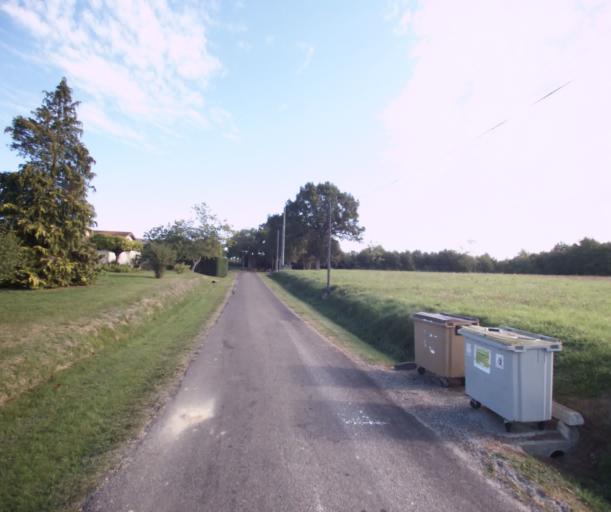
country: FR
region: Midi-Pyrenees
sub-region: Departement du Gers
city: Cazaubon
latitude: 43.8911
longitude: 0.0029
